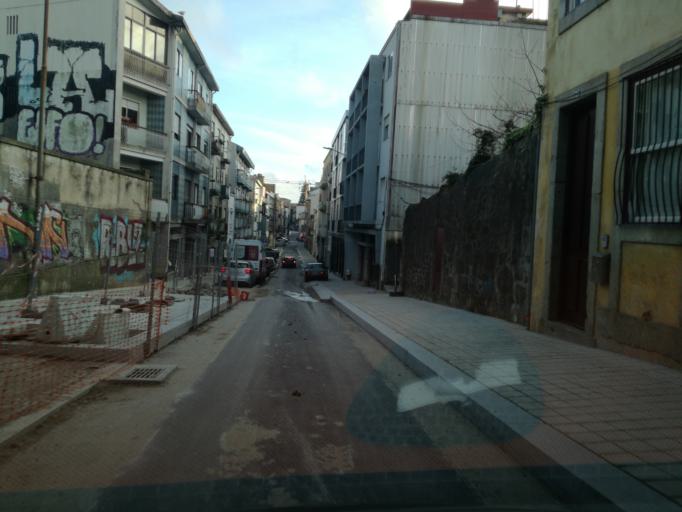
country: PT
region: Porto
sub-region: Porto
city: Porto
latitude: 41.1580
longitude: -8.6198
